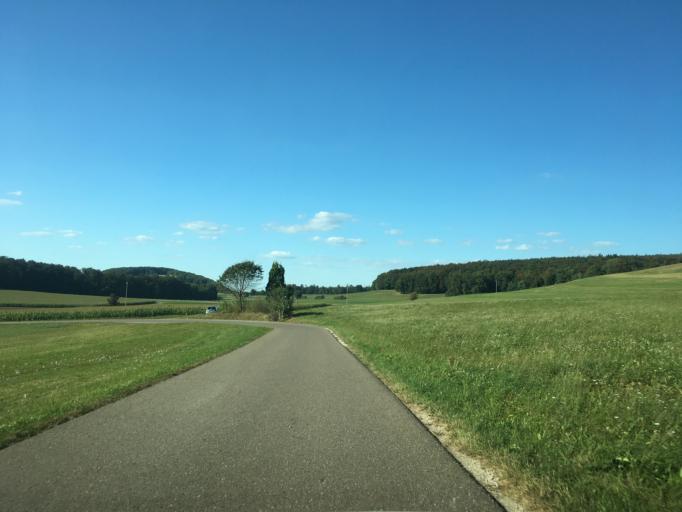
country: DE
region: Baden-Wuerttemberg
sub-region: Tuebingen Region
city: Pfullingen
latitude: 48.4130
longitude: 9.2140
